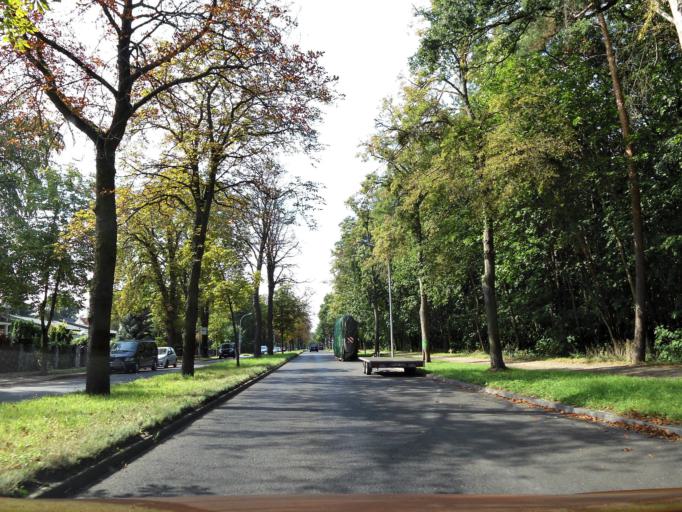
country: DE
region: Berlin
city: Lichterfelde
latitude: 52.4088
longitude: 13.2900
